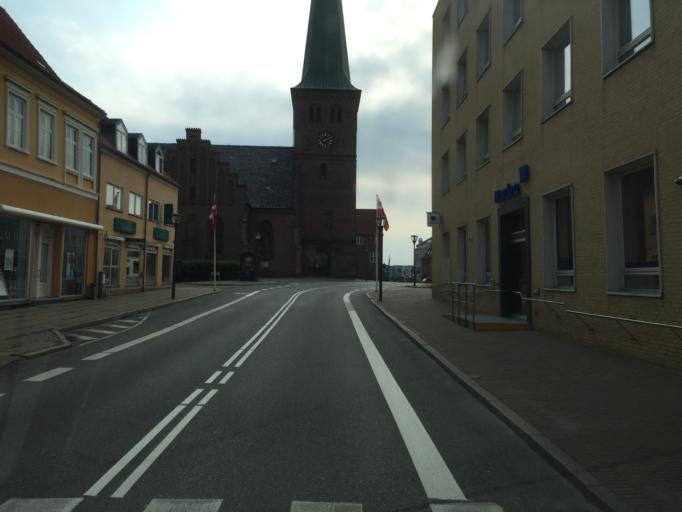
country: DK
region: South Denmark
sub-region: Nyborg Kommune
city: Nyborg
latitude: 55.3122
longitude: 10.7929
